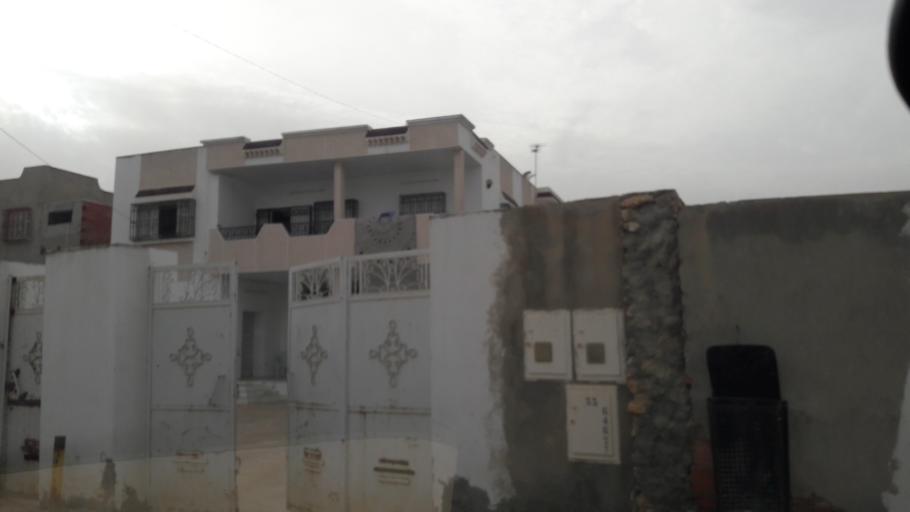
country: TN
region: Safaqis
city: Al Qarmadah
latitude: 34.7774
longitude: 10.7640
